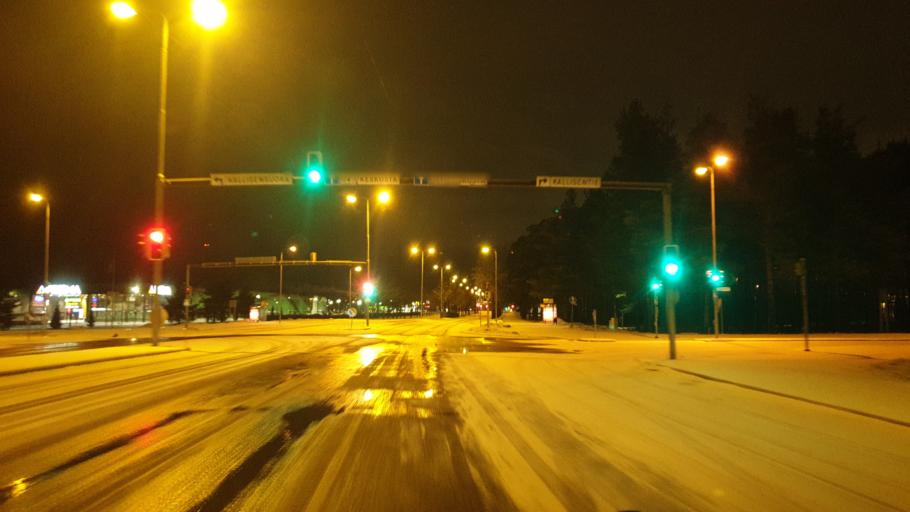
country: FI
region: Northern Ostrobothnia
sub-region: Oulu
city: Oulu
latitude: 64.9919
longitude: 25.4656
